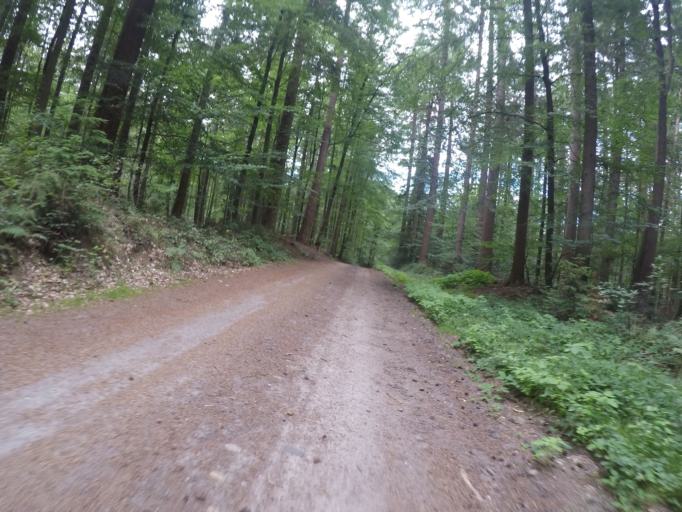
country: DE
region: Lower Saxony
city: Wingst
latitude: 53.7299
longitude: 9.0694
